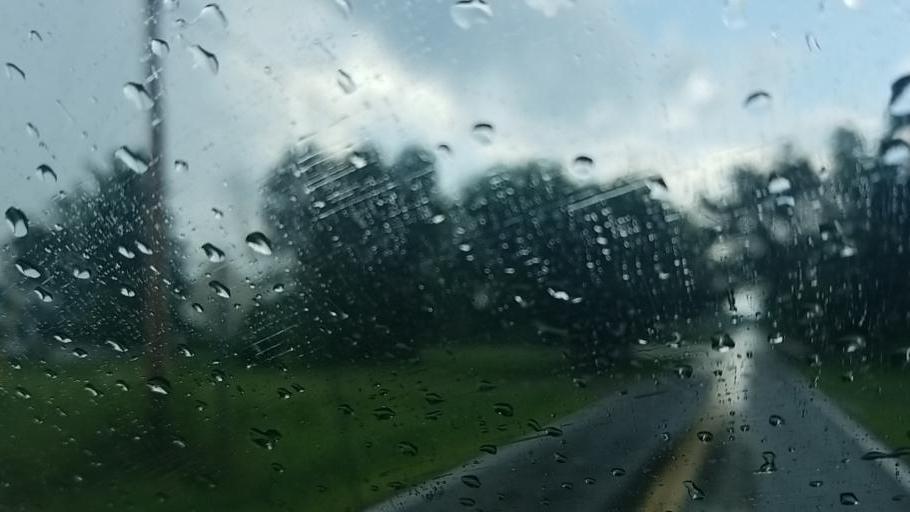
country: US
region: Ohio
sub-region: Lorain County
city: Lagrange
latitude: 41.2241
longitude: -82.0748
